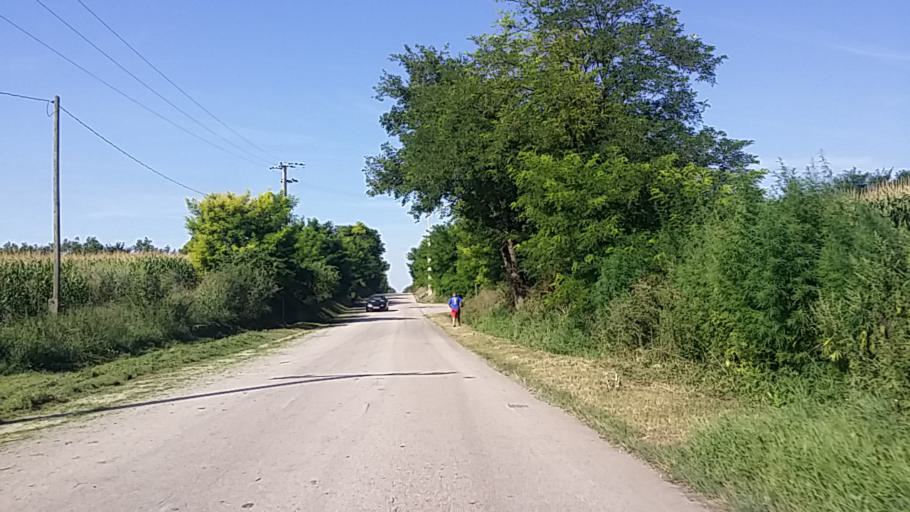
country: HU
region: Fejer
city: Ivancsa
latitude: 47.1368
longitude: 18.8294
